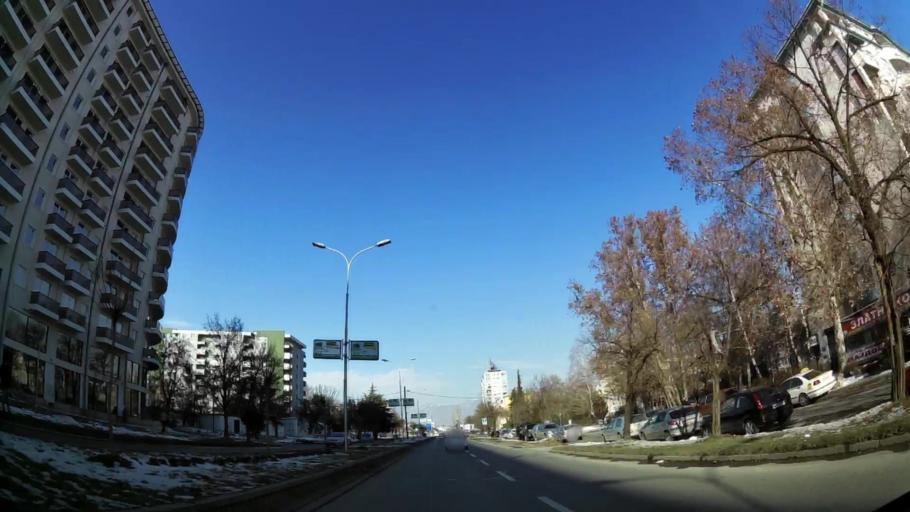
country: MK
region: Karpos
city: Skopje
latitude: 41.9995
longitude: 21.4042
